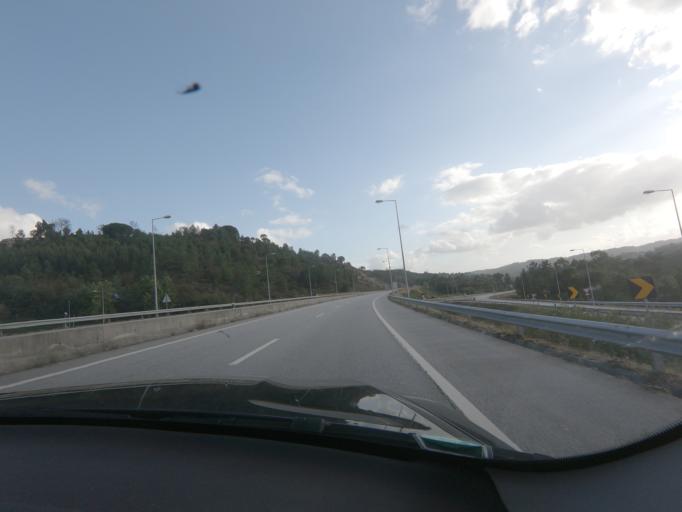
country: PT
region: Viseu
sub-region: Viseu
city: Viseu
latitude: 40.6138
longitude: -7.9642
